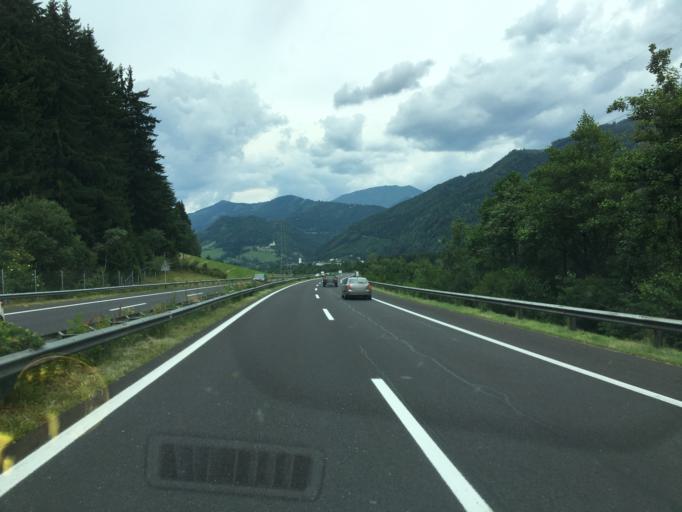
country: AT
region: Styria
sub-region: Politischer Bezirk Leoben
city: Kalwang
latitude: 47.4084
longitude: 14.7733
